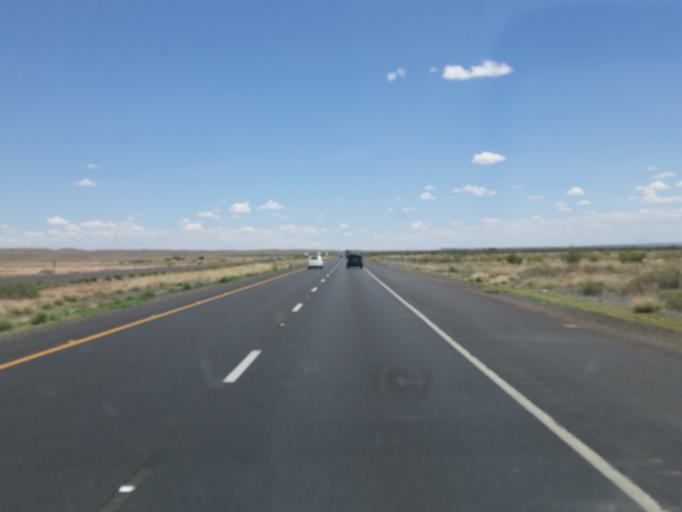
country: US
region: Arizona
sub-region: Navajo County
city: Winslow
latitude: 34.9968
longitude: -110.5892
